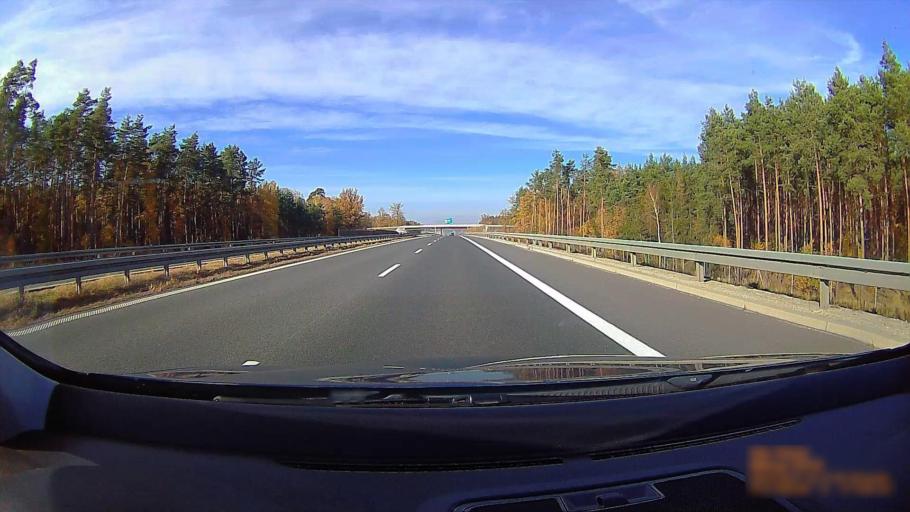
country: PL
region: Greater Poland Voivodeship
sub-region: Powiat ostrowski
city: Ostrow Wielkopolski
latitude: 51.6530
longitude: 17.8682
